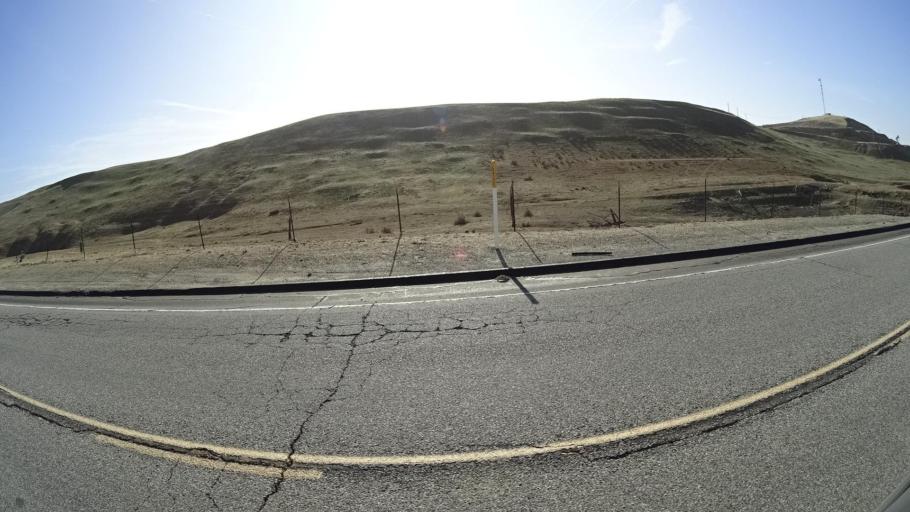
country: US
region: California
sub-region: Kern County
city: Oildale
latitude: 35.4904
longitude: -119.0007
